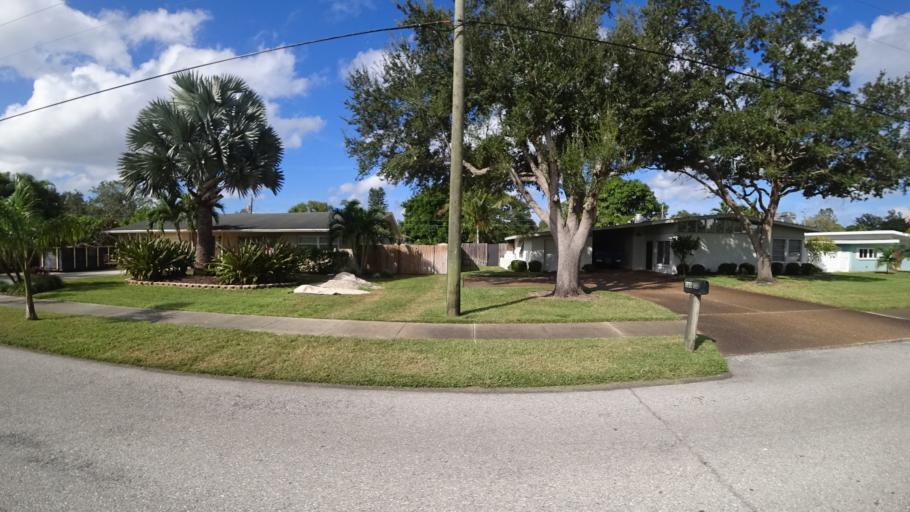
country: US
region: Florida
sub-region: Manatee County
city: West Bradenton
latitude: 27.5019
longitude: -82.6079
